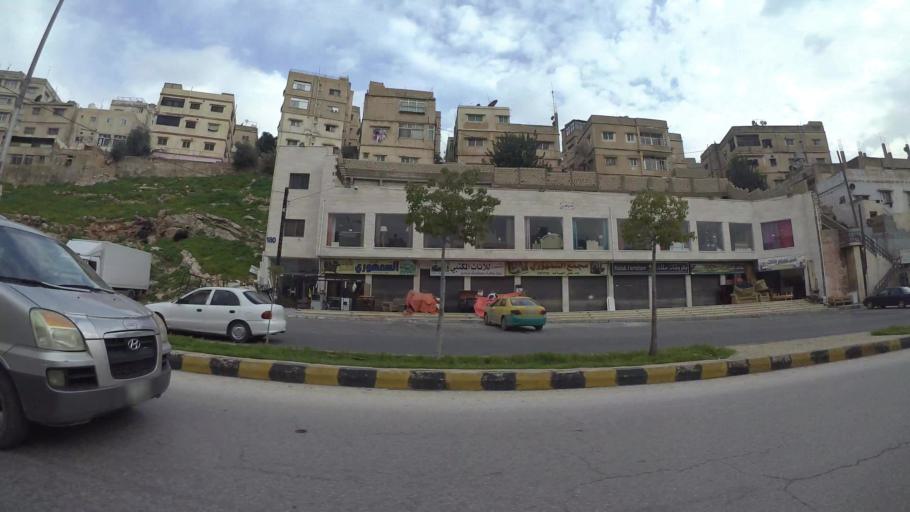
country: JO
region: Amman
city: Amman
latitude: 31.9659
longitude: 35.9320
